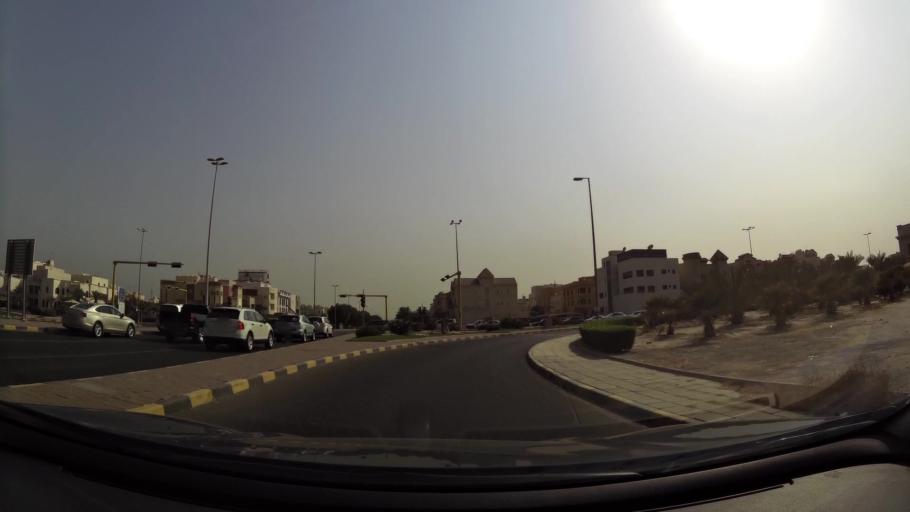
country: KW
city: Bayan
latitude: 29.2855
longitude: 48.0514
